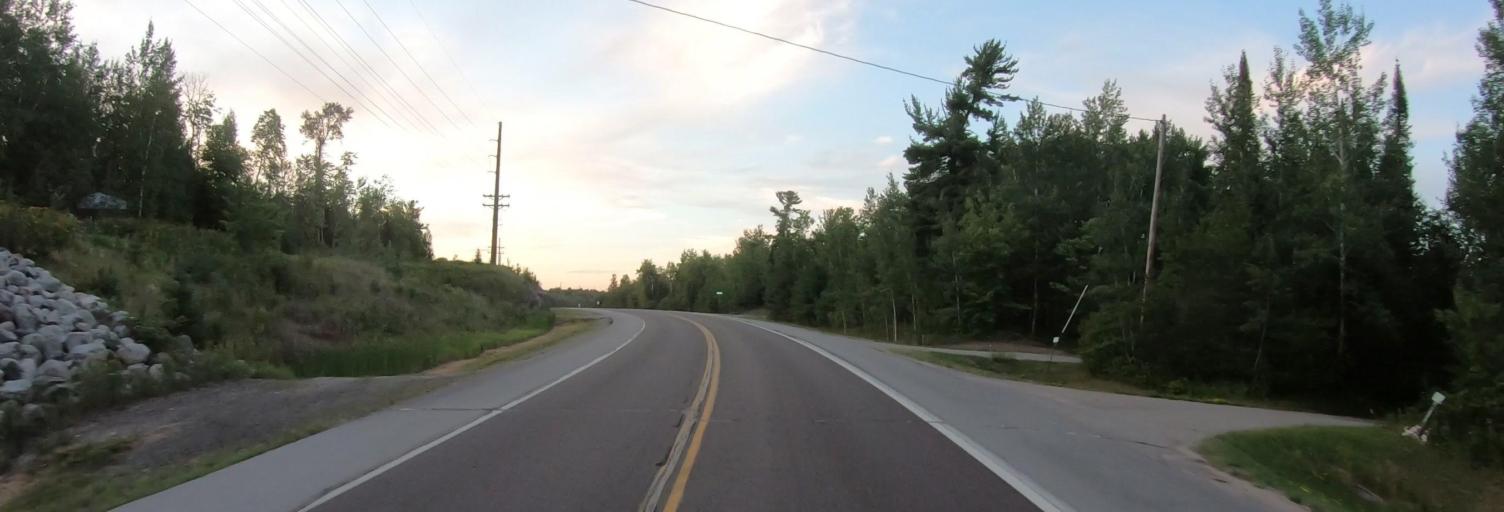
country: US
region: Minnesota
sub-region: Saint Louis County
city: Aurora
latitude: 47.8023
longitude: -92.3715
